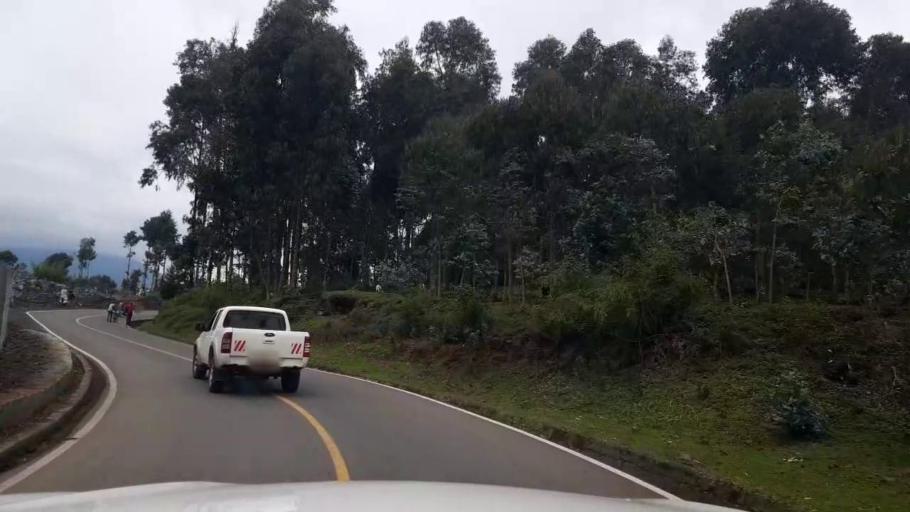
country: RW
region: Northern Province
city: Musanze
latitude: -1.4302
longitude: 29.5636
